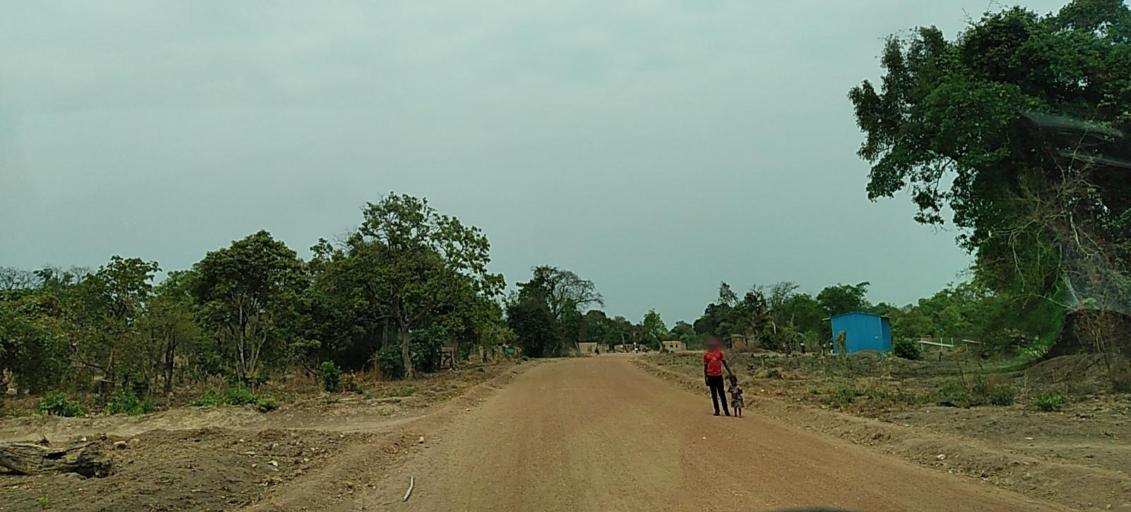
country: ZM
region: North-Western
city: Solwezi
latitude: -12.4760
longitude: 26.5293
